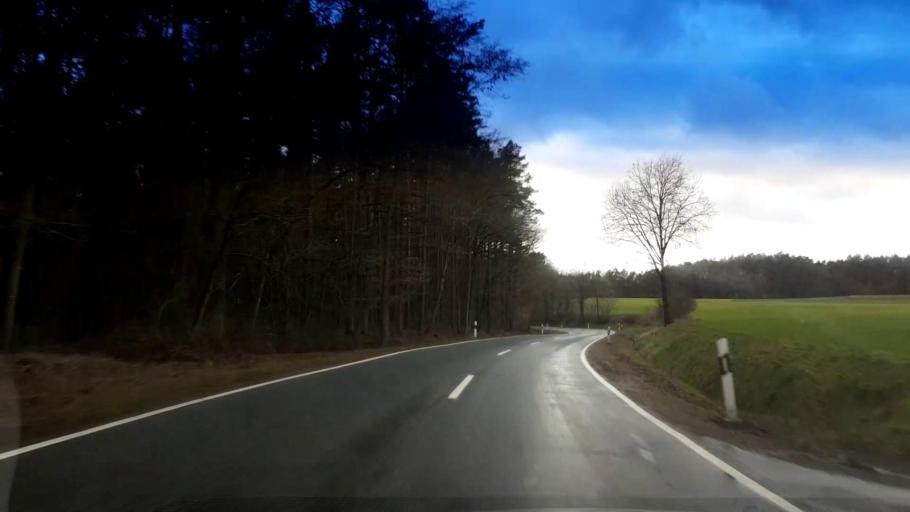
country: DE
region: Bavaria
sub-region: Upper Franconia
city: Lauter
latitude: 49.9636
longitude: 10.7741
